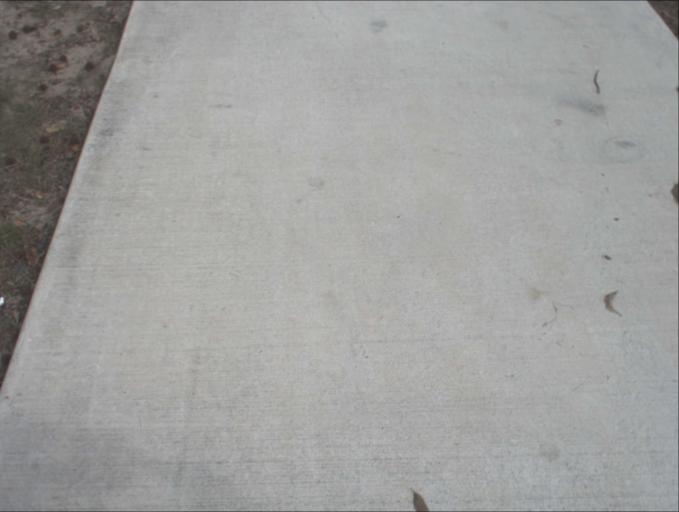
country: AU
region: Queensland
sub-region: Logan
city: Logan Reserve
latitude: -27.6842
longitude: 153.0930
